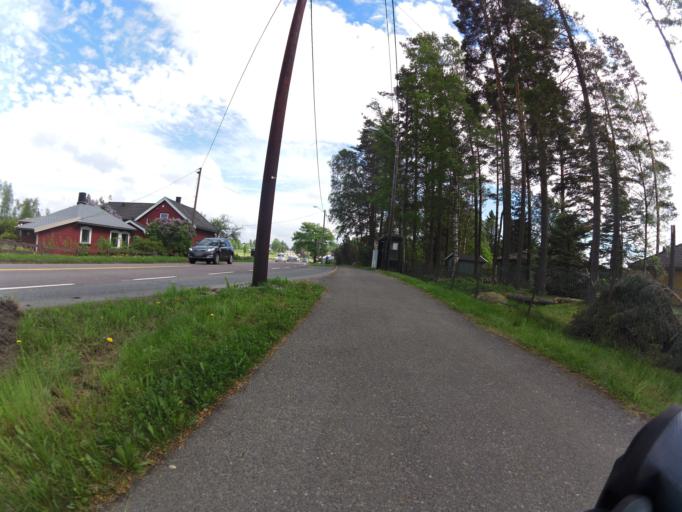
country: NO
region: Ostfold
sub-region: Rade
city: Karlshus
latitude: 59.3548
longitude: 10.8482
